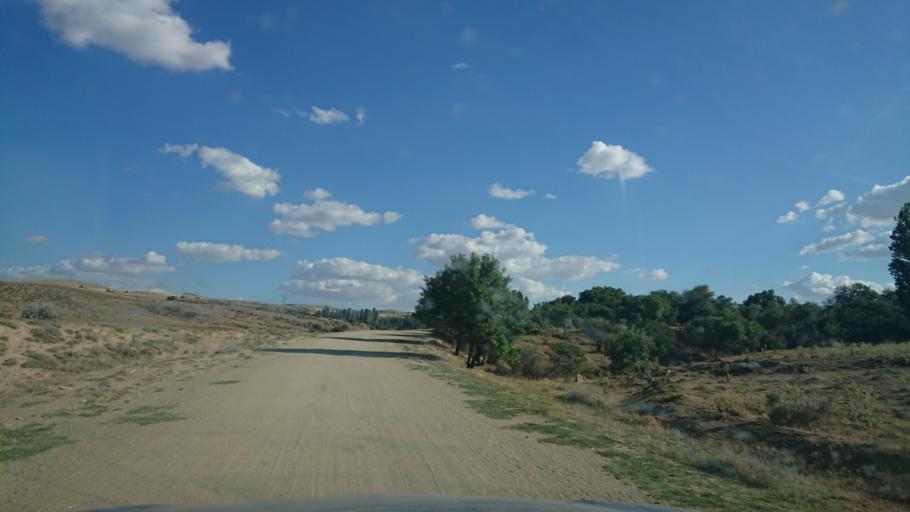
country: TR
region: Aksaray
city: Sariyahsi
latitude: 38.9455
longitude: 33.8801
